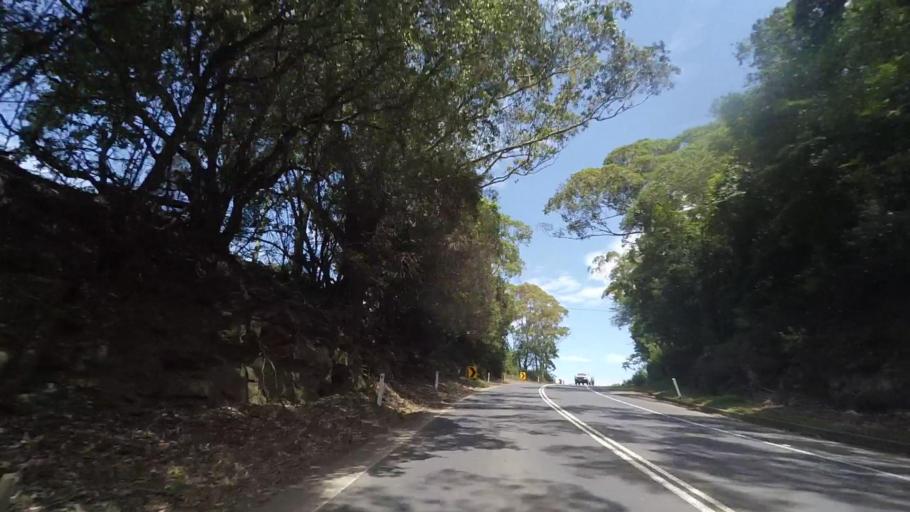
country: AU
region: New South Wales
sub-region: Shoalhaven Shire
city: Berry
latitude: -34.7566
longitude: 150.7482
